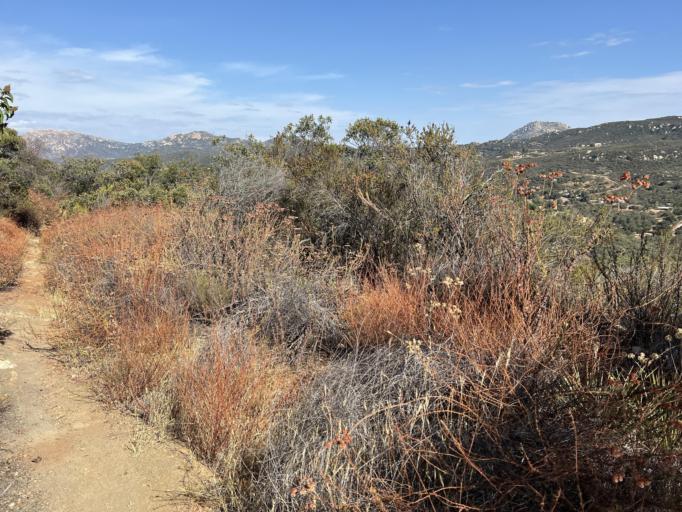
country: US
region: California
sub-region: San Diego County
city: Harbison Canyon
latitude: 32.7485
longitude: -116.8004
